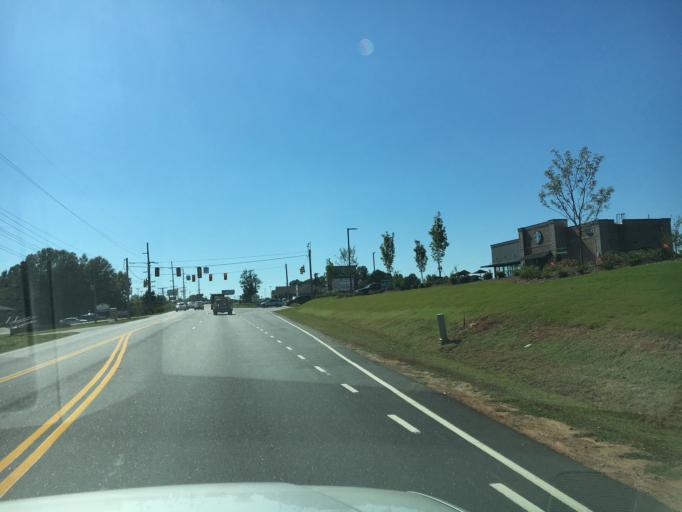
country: US
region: South Carolina
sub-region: Greenville County
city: Five Forks
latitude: 34.8066
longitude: -82.2237
